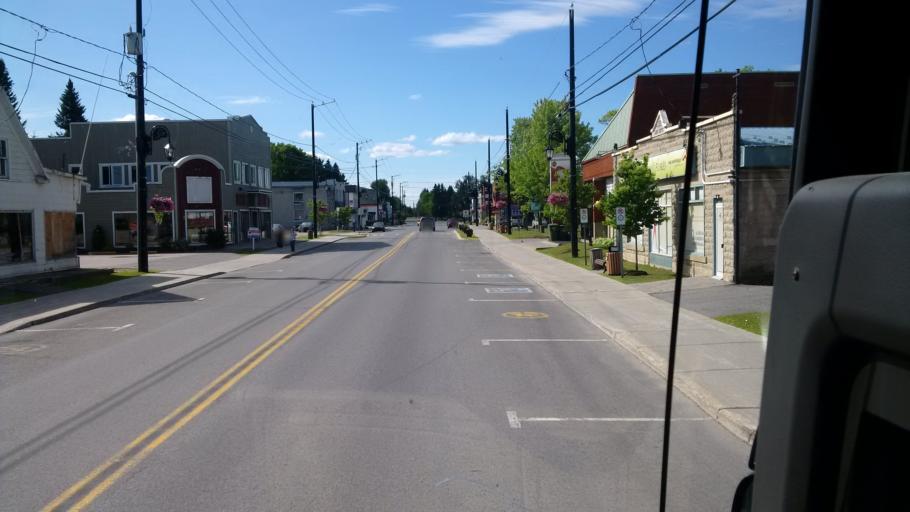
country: CA
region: Quebec
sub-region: Laurentides
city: Riviere-Rouge
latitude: 46.4144
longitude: -74.8714
